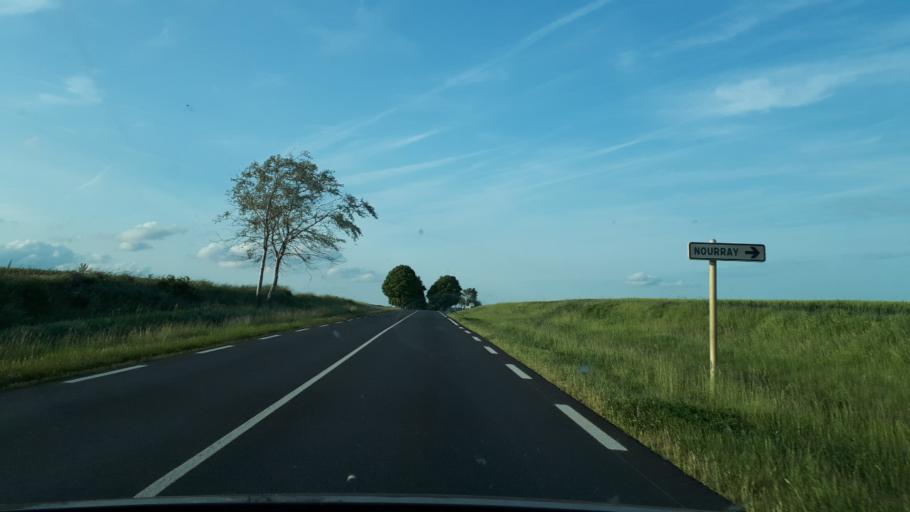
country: FR
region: Centre
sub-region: Departement du Loir-et-Cher
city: Saint-Amand-Longpre
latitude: 47.7378
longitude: 1.0329
